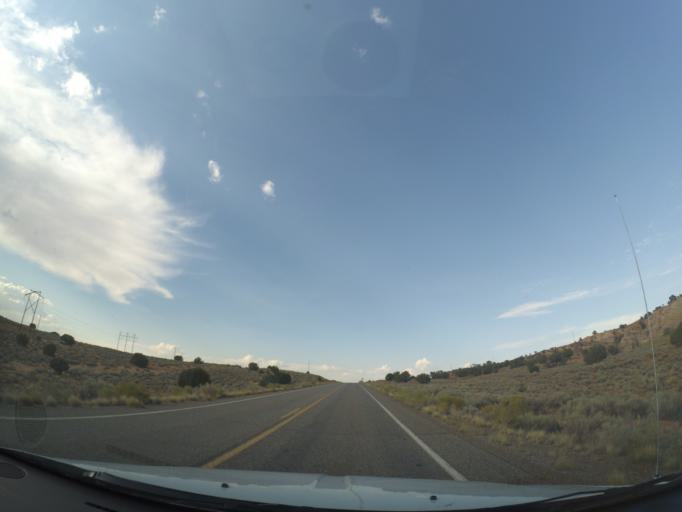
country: US
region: Arizona
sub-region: Coconino County
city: LeChee
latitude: 36.7079
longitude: -111.4428
